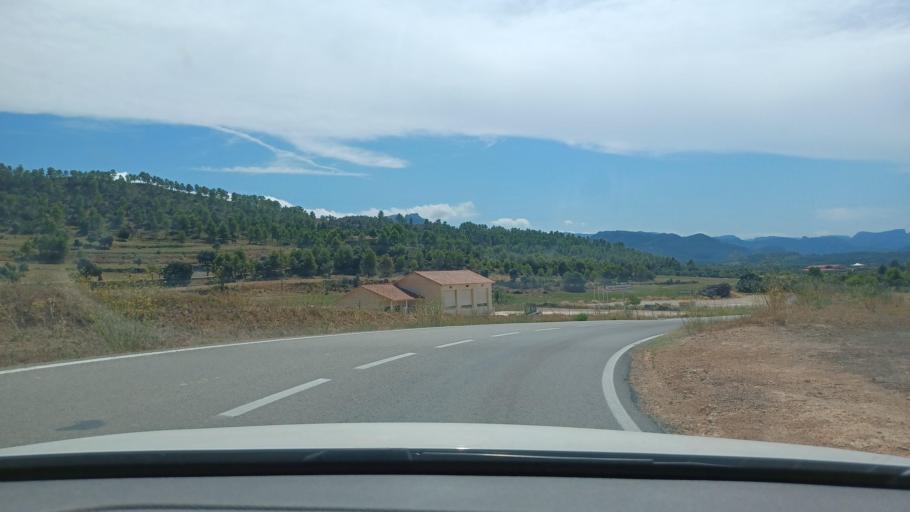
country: ES
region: Catalonia
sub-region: Provincia de Tarragona
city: Horta de Sant Joan
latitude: 40.9496
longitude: 0.3208
